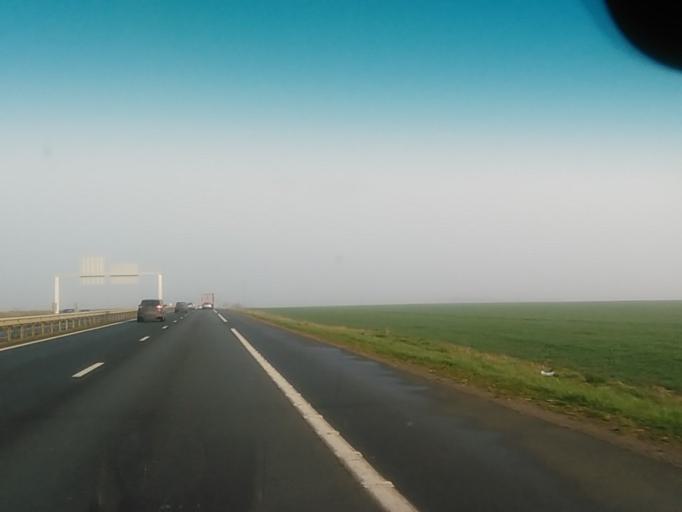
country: FR
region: Lower Normandy
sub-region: Departement du Calvados
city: Bourguebus
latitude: 49.1080
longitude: -0.3172
